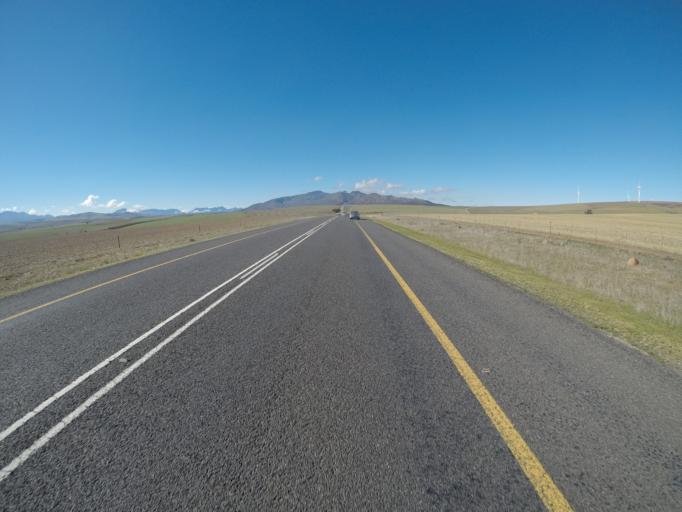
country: ZA
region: Western Cape
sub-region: Overberg District Municipality
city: Caledon
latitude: -34.2115
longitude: 19.3652
